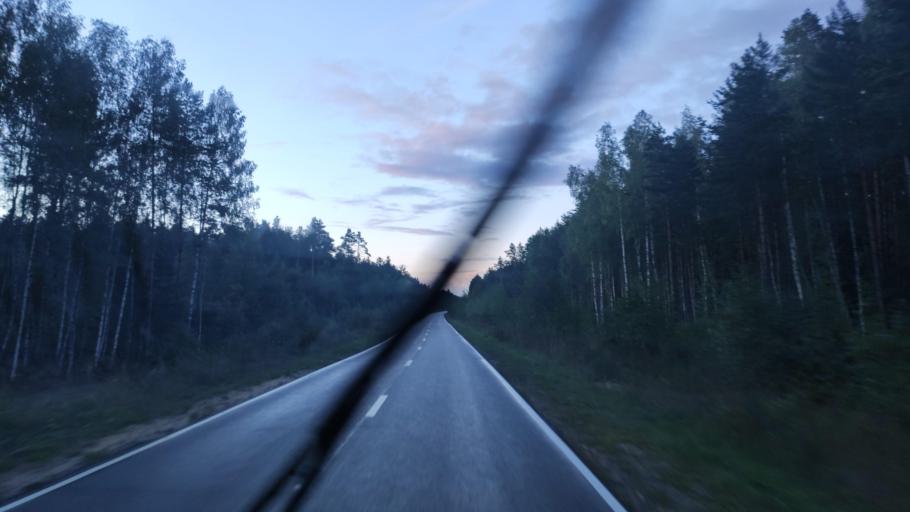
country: RU
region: Vladimir
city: Galitsy
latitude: 56.0206
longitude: 42.8602
